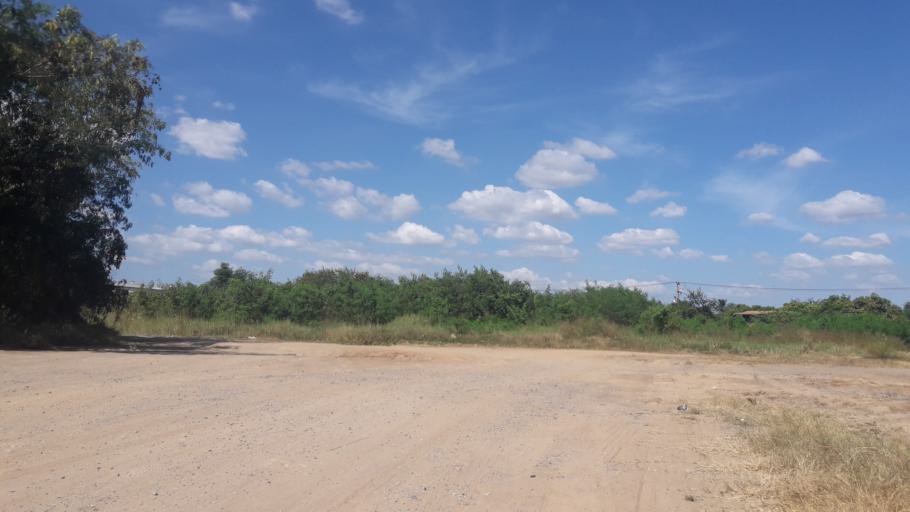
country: TH
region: Phichit
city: Thap Khlo
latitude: 16.1671
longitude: 100.5819
